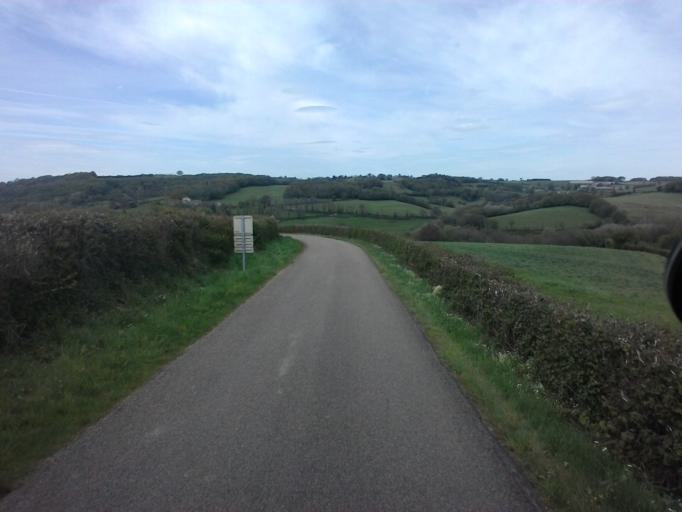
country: FR
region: Bourgogne
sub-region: Departement de l'Yonne
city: Avallon
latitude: 47.3745
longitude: 3.9412
